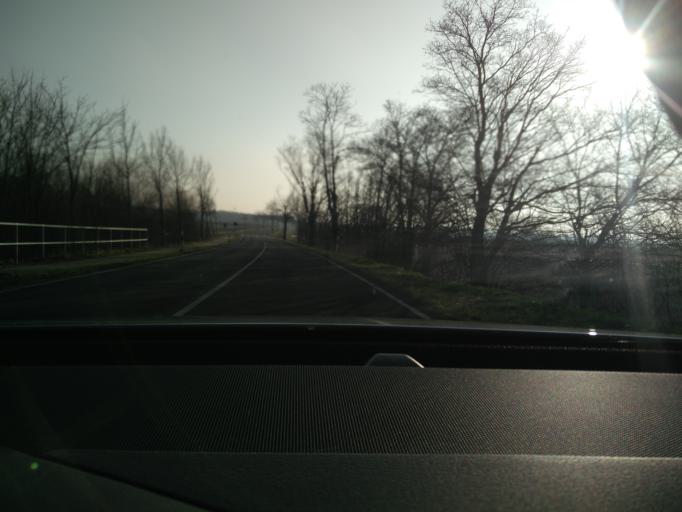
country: DE
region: Lower Saxony
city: Dollbergen
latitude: 52.3596
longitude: 10.1535
